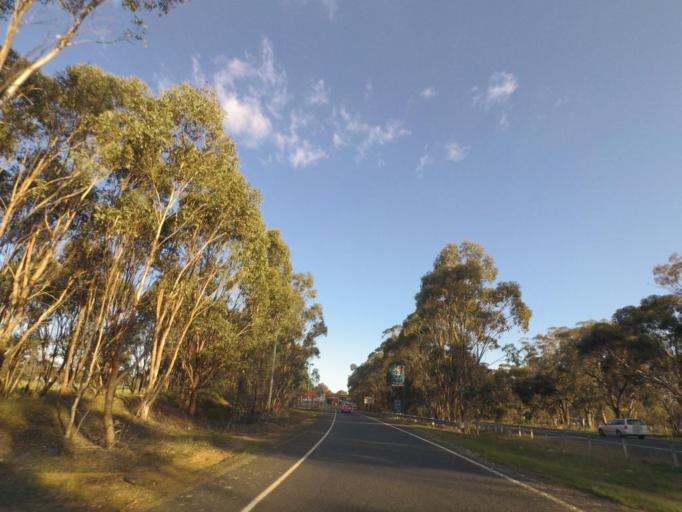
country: AU
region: Victoria
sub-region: Murrindindi
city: Kinglake West
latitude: -37.0613
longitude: 145.1013
